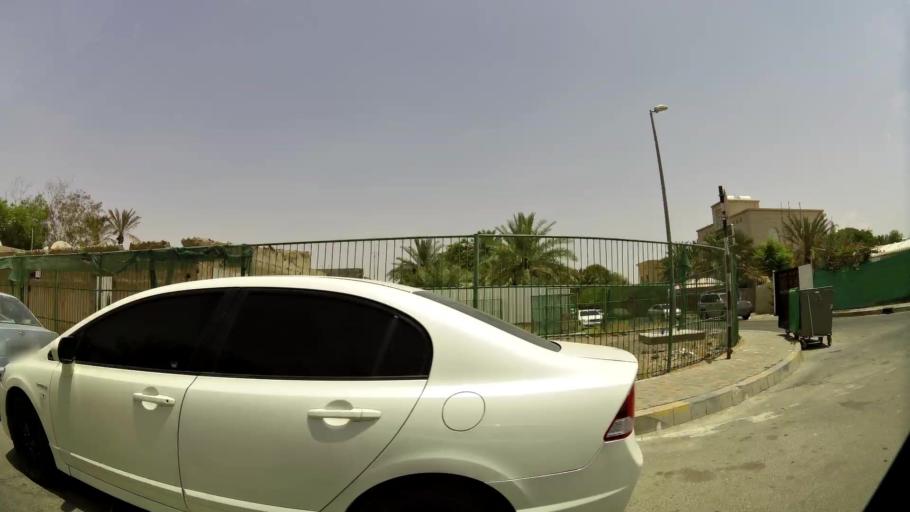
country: AE
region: Abu Dhabi
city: Al Ain
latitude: 24.1994
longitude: 55.7728
